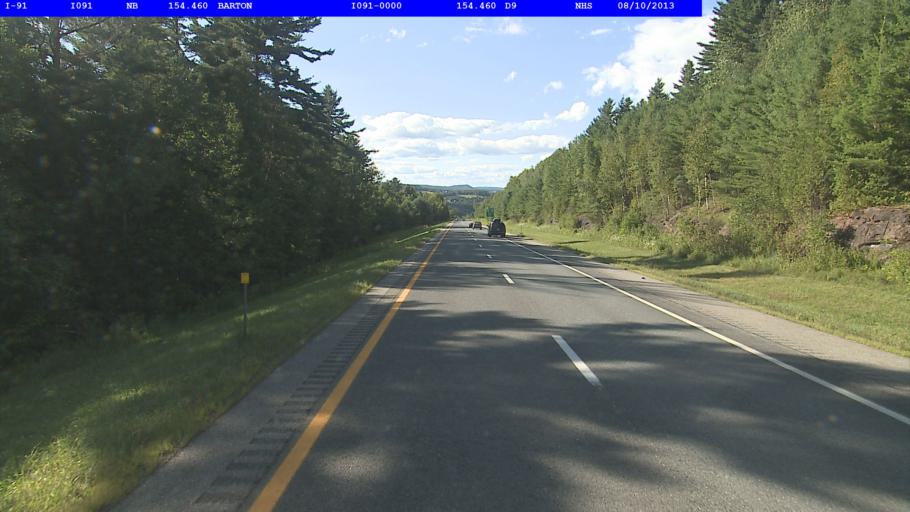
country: US
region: Vermont
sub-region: Orleans County
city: Newport
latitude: 44.7157
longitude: -72.1740
